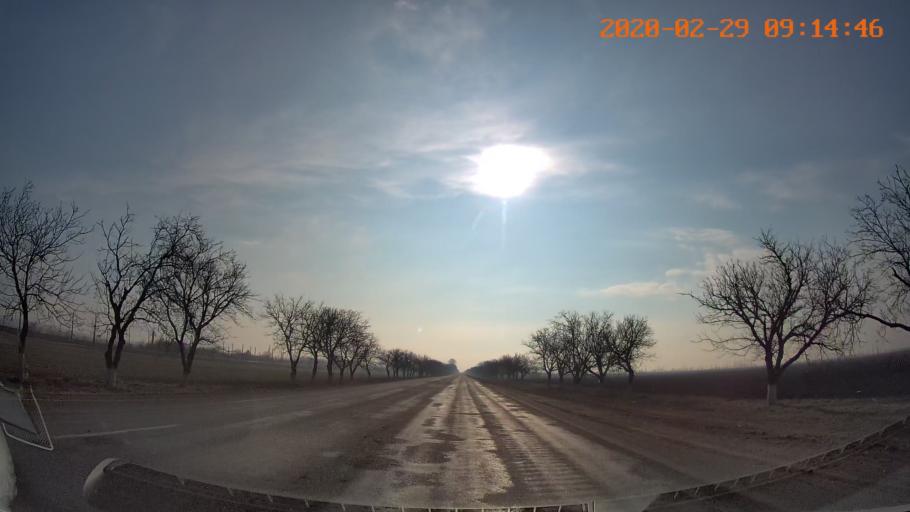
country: MD
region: Telenesti
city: Pervomaisc
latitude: 46.8059
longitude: 29.8584
